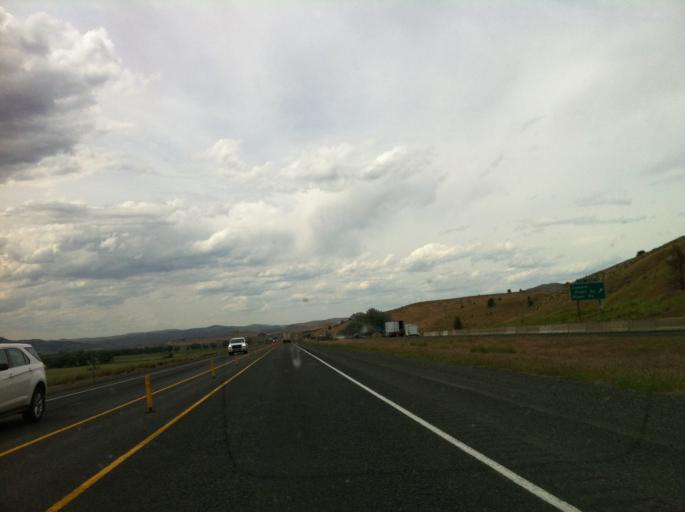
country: US
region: Oregon
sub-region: Baker County
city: Baker City
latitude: 44.5449
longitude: -117.4190
